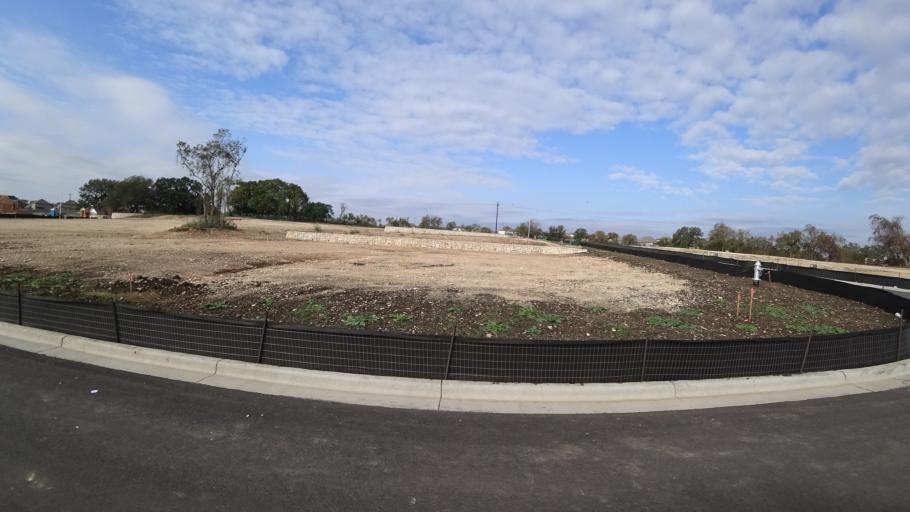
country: US
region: Texas
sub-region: Travis County
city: Manchaca
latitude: 30.1323
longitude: -97.8445
